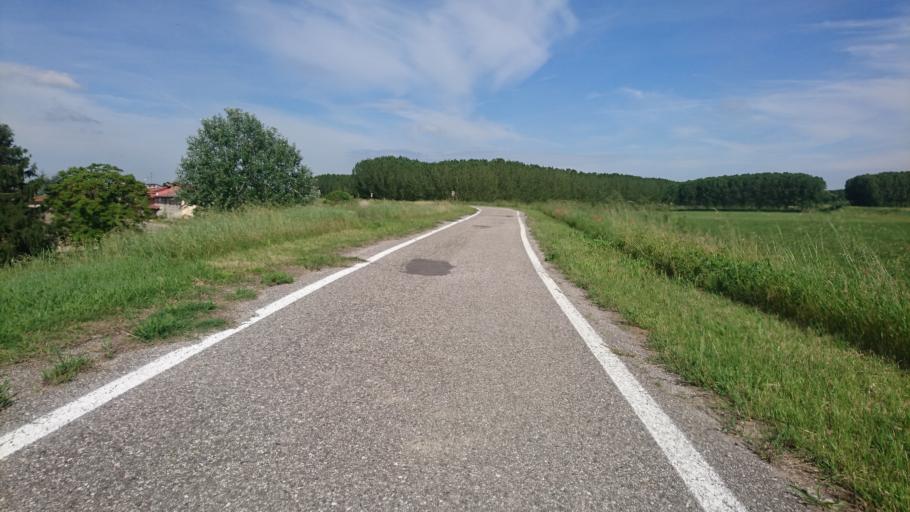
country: IT
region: Lombardy
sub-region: Provincia di Mantova
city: Carbonara di Po
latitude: 45.0382
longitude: 11.2314
